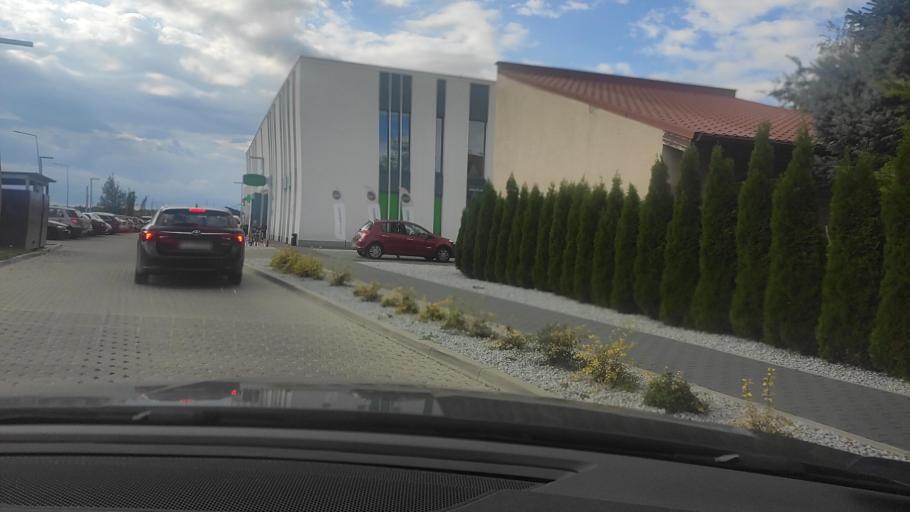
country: PL
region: Greater Poland Voivodeship
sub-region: Powiat poznanski
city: Swarzedz
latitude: 52.3898
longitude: 17.0713
